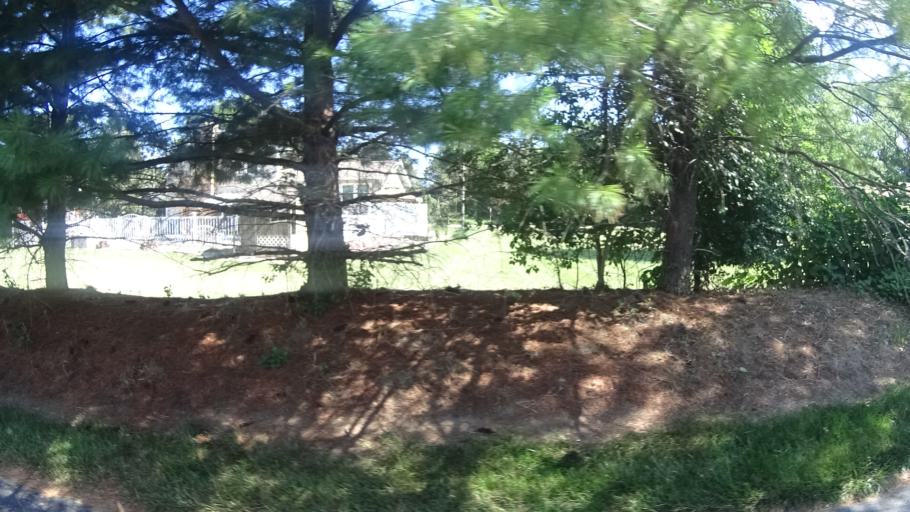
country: US
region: Ohio
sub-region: Erie County
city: Sandusky
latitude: 41.4118
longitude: -82.6578
